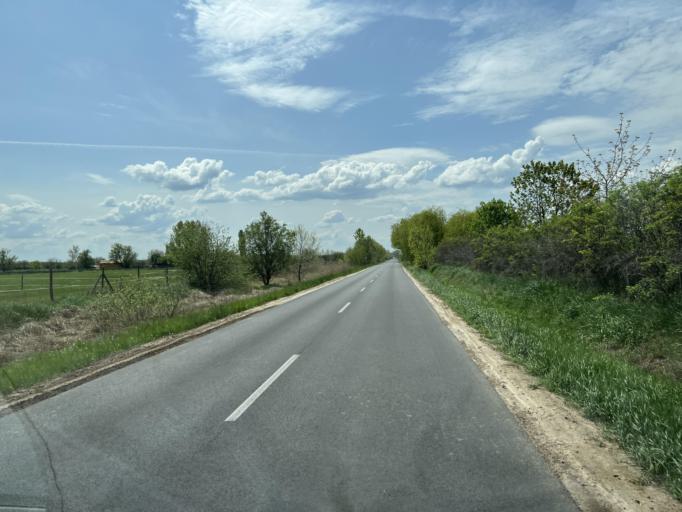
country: HU
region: Pest
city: Cegled
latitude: 47.1571
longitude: 19.7696
